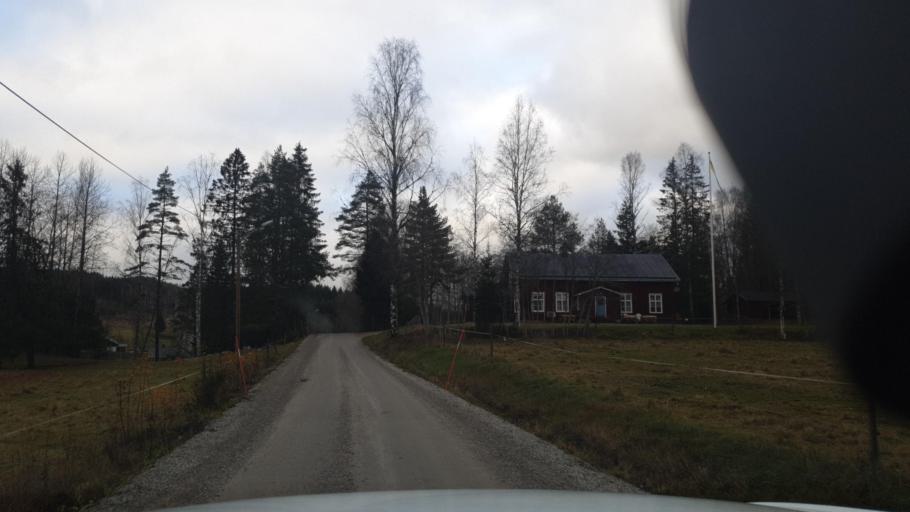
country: SE
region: Vaermland
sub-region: Arvika Kommun
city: Arvika
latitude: 59.6744
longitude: 12.7683
